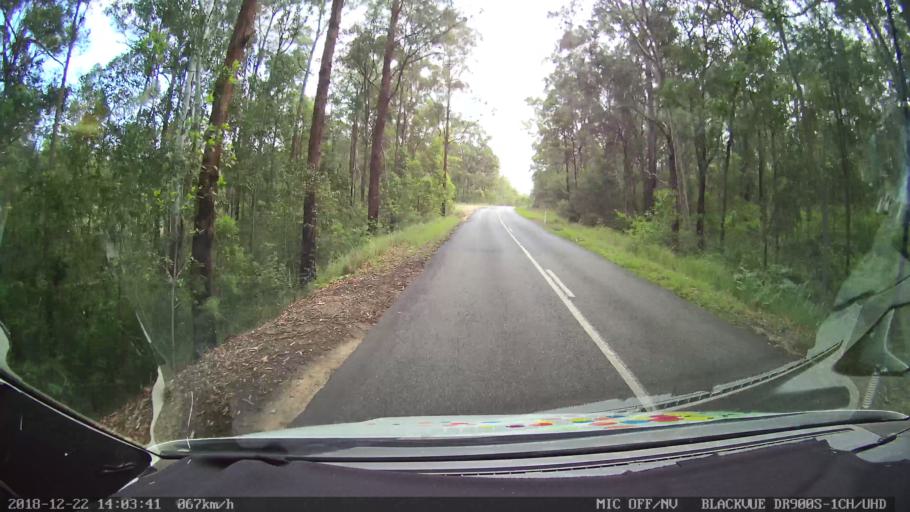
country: AU
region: New South Wales
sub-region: Clarence Valley
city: Coutts Crossing
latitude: -29.9311
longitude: 152.7358
